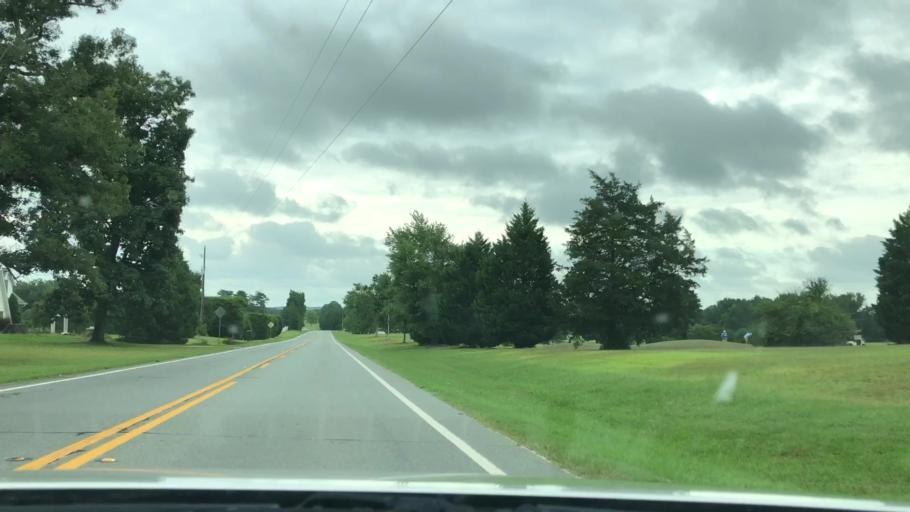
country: US
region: Georgia
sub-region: Pike County
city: Zebulon
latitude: 33.1110
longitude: -84.3930
